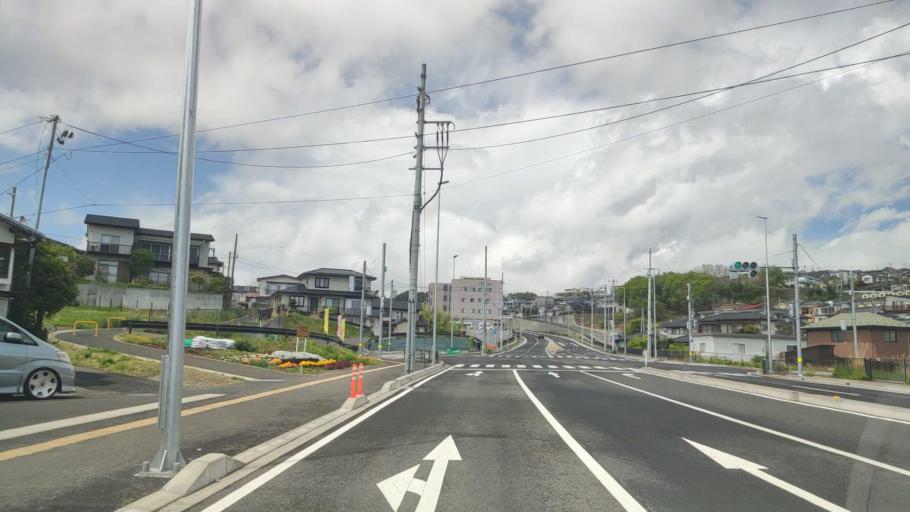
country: JP
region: Miyagi
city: Sendai
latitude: 38.2329
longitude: 140.8532
